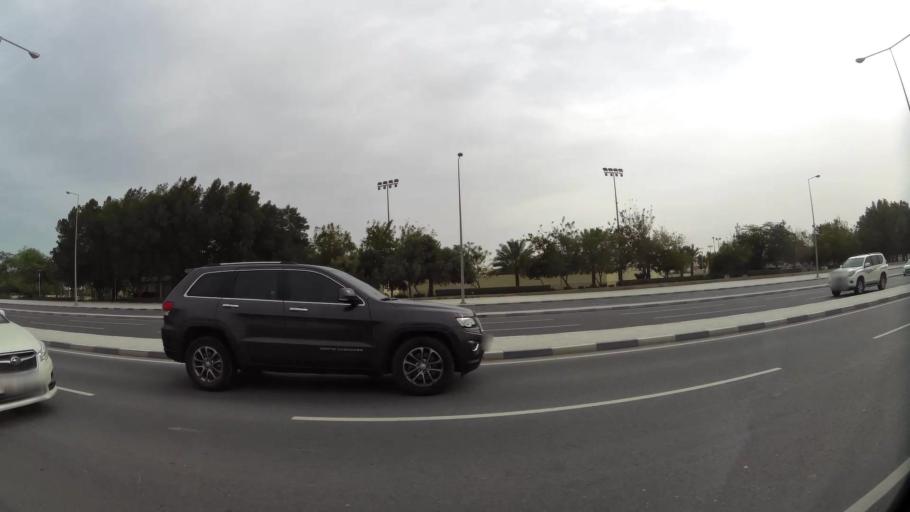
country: QA
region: Baladiyat ar Rayyan
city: Ar Rayyan
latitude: 25.3353
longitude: 51.4792
